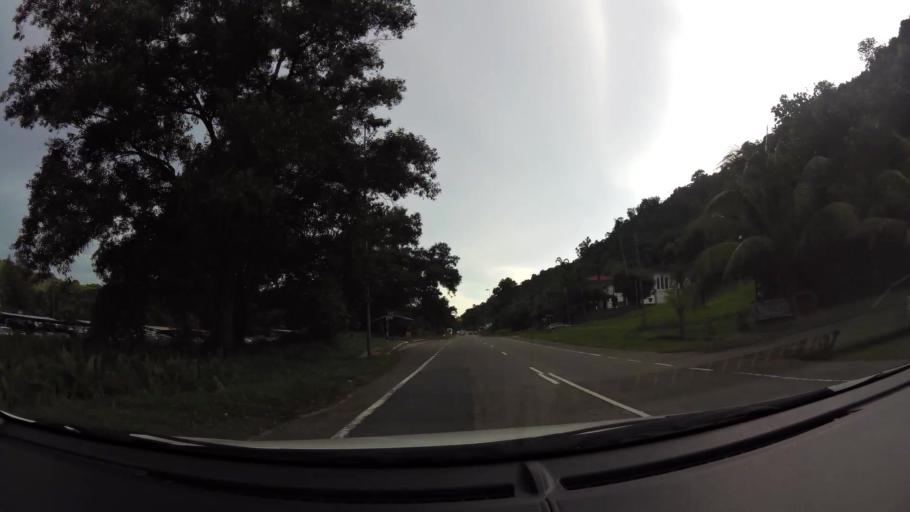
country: BN
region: Brunei and Muara
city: Bandar Seri Begawan
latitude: 4.9181
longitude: 115.0069
